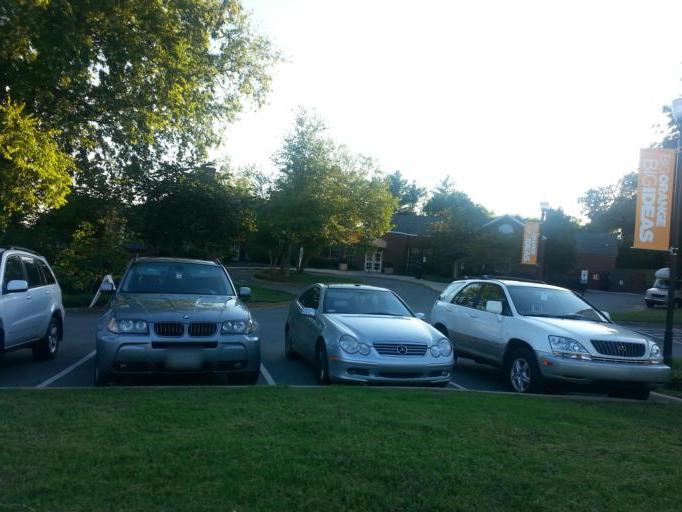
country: US
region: Tennessee
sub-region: Knox County
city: Knoxville
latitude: 35.9506
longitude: -83.9467
